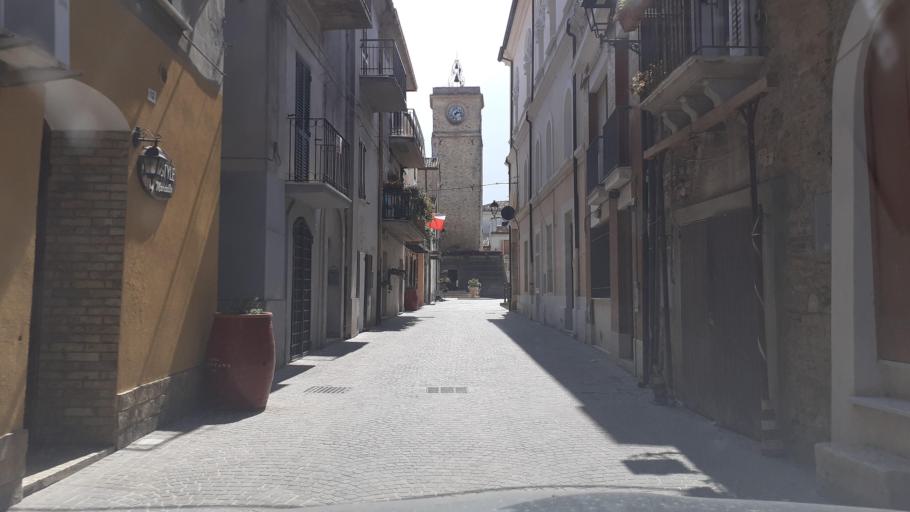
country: IT
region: Abruzzo
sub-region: Provincia di Chieti
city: Rocca San Giovanni
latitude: 42.2511
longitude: 14.4653
